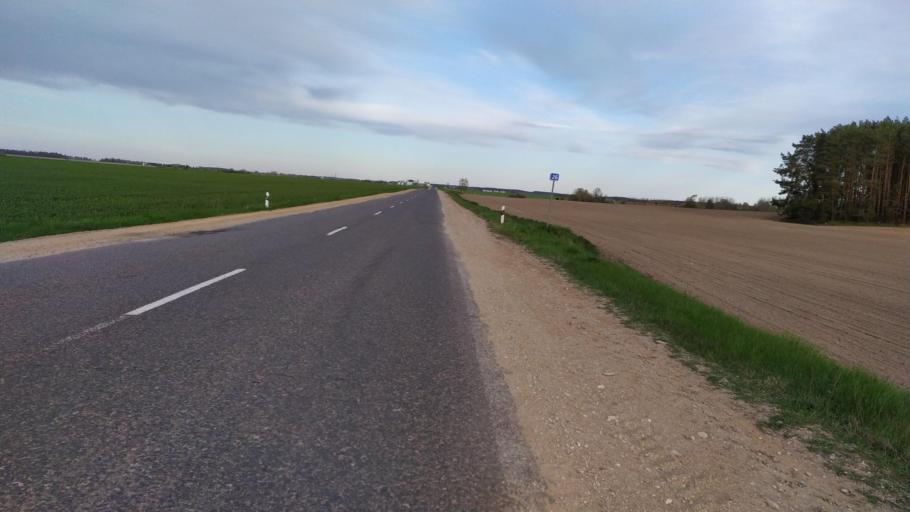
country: BY
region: Brest
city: Kamyanyets
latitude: 52.4070
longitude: 23.7424
